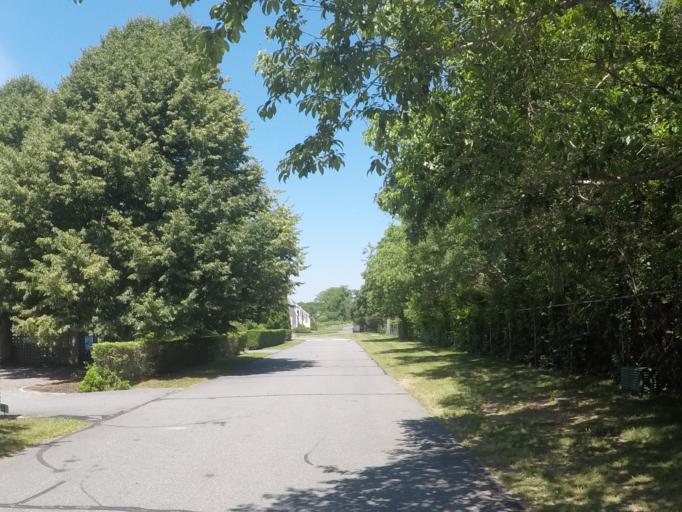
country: US
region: Massachusetts
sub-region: Bristol County
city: Bliss Corner
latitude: 41.5450
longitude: -70.9373
